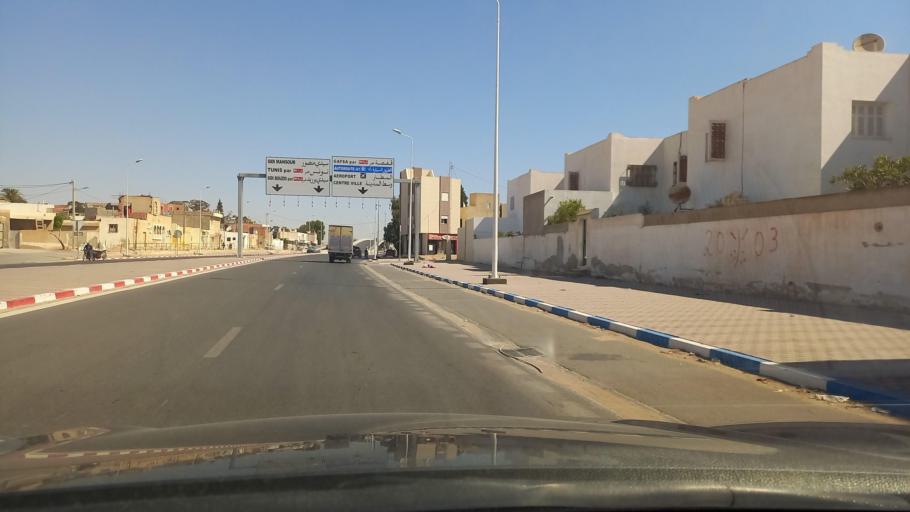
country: TN
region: Safaqis
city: Sfax
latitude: 34.7300
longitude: 10.7254
